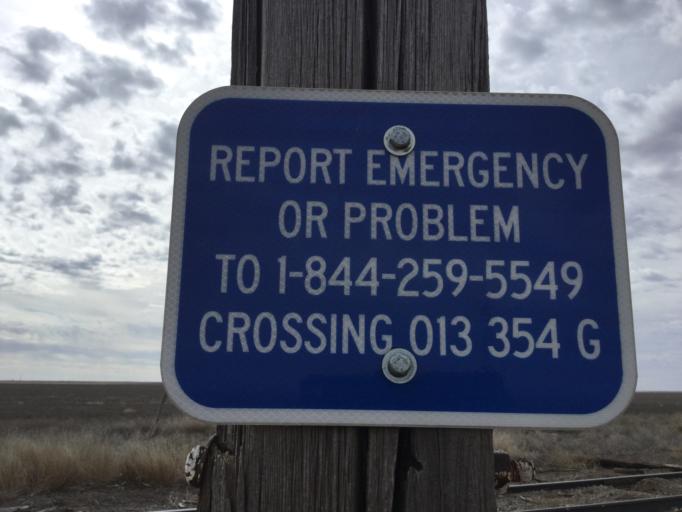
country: US
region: Kansas
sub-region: Stanton County
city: Johnson
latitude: 37.4768
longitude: -102.0206
